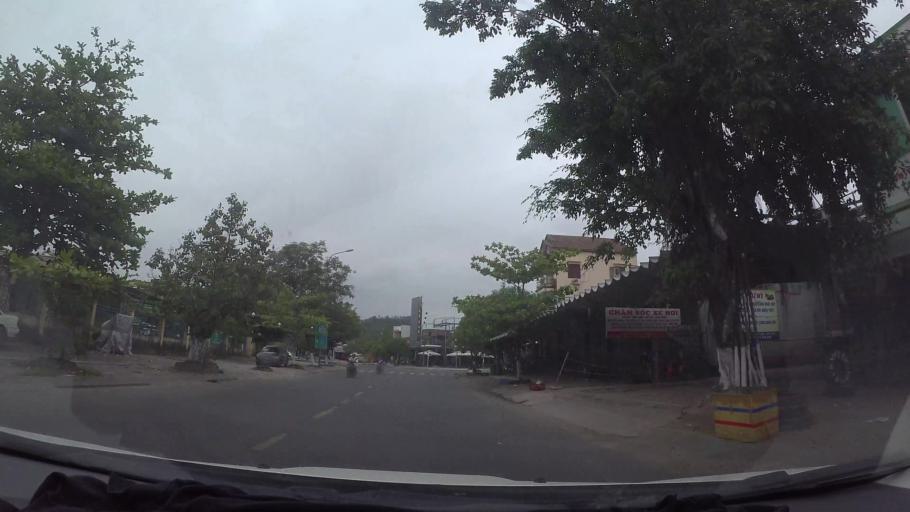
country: VN
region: Da Nang
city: Lien Chieu
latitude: 16.0679
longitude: 108.1485
